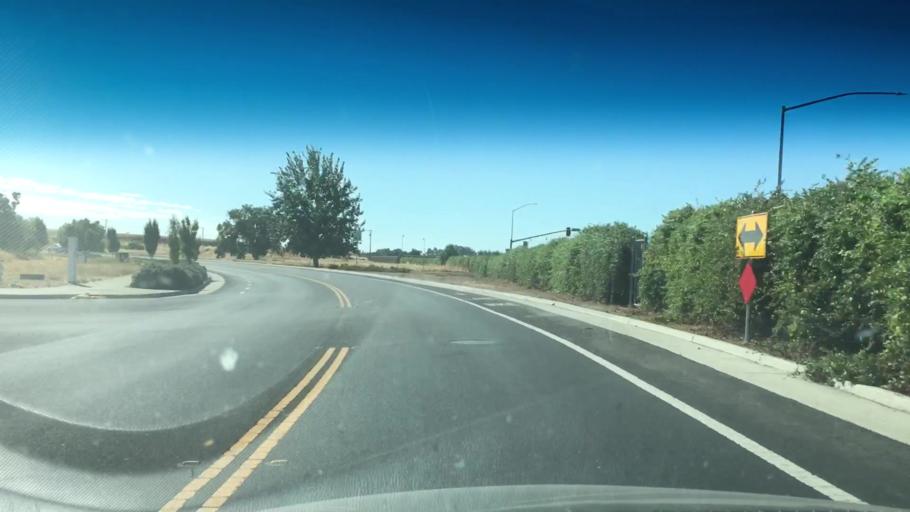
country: US
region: California
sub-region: Sacramento County
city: Laguna
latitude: 38.4409
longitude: -121.4025
